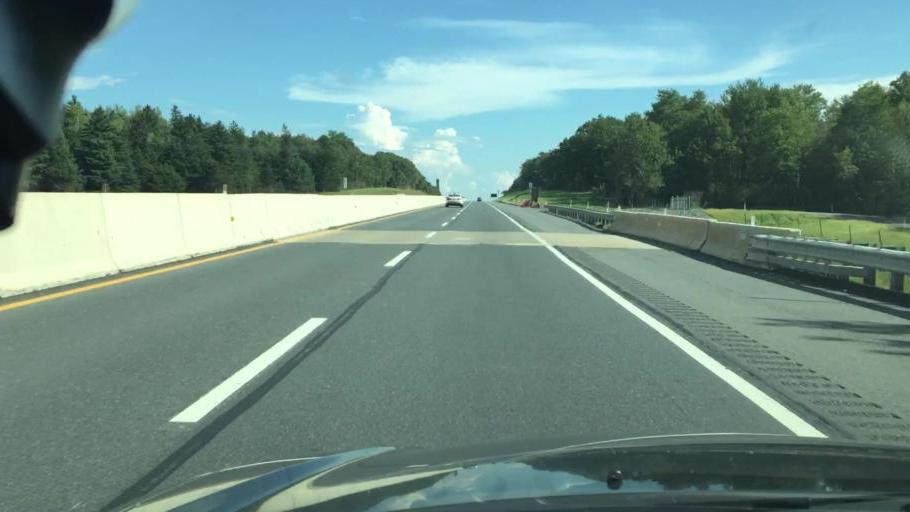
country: US
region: Pennsylvania
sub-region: Carbon County
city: Towamensing Trails
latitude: 41.0357
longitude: -75.6592
